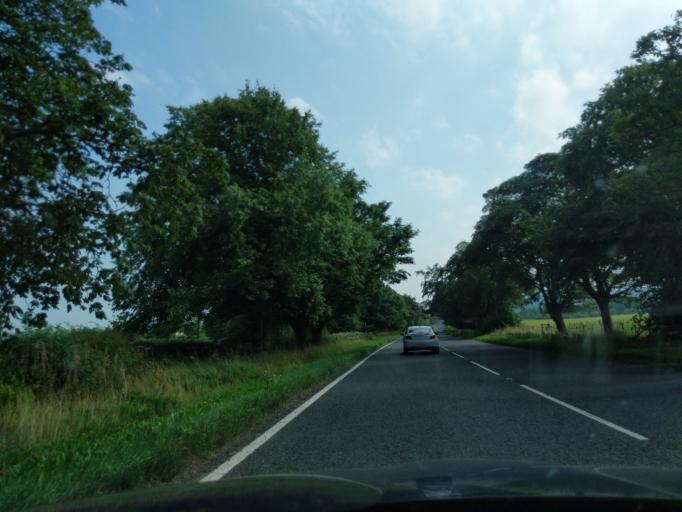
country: GB
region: England
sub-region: Northumberland
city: Longhorsley
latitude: 55.2988
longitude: -1.7896
